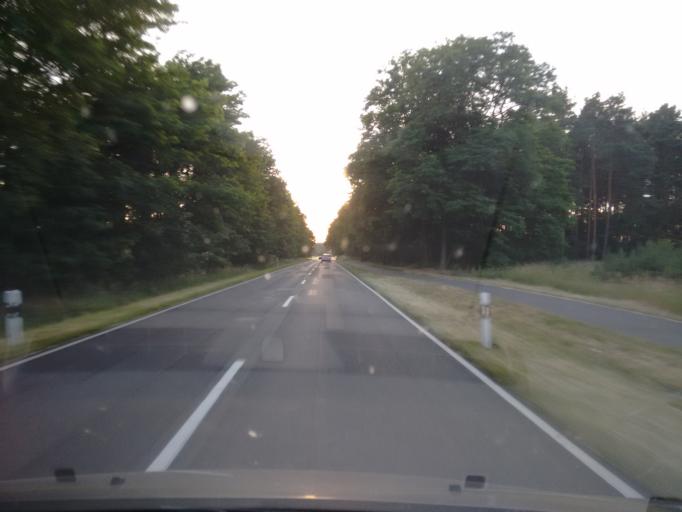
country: DE
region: Brandenburg
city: Mixdorf
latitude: 52.1380
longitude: 14.4279
